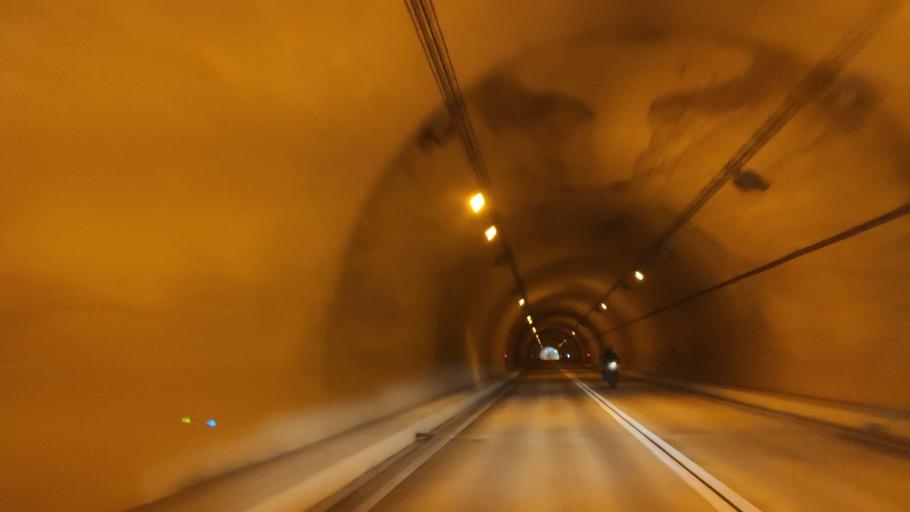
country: JP
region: Kyoto
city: Fukuchiyama
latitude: 35.2121
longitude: 134.9433
